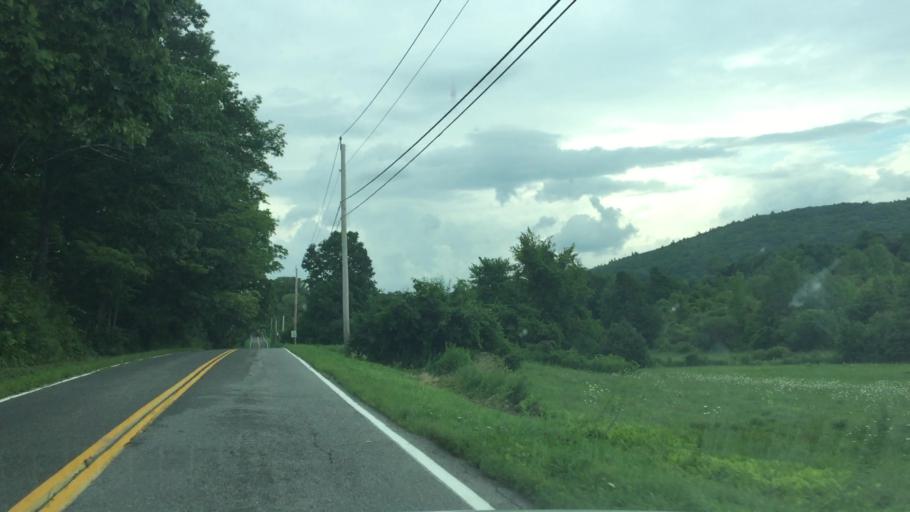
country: US
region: Massachusetts
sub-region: Berkshire County
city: Housatonic
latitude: 42.2988
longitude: -73.4030
